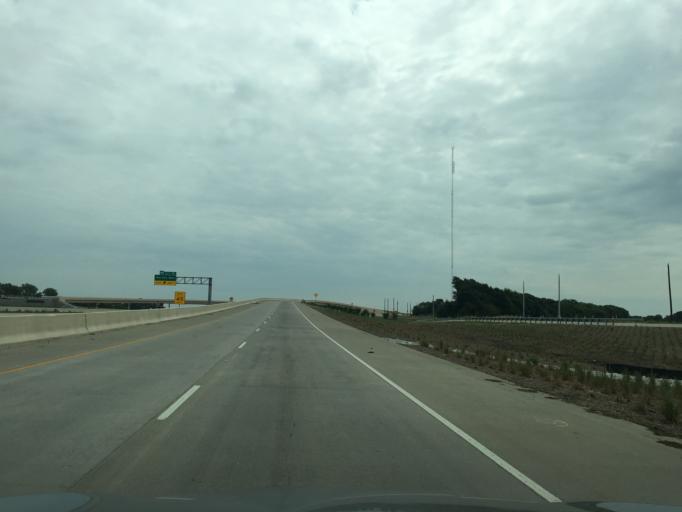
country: US
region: Texas
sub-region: Collin County
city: Melissa
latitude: 33.2623
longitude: -96.6023
